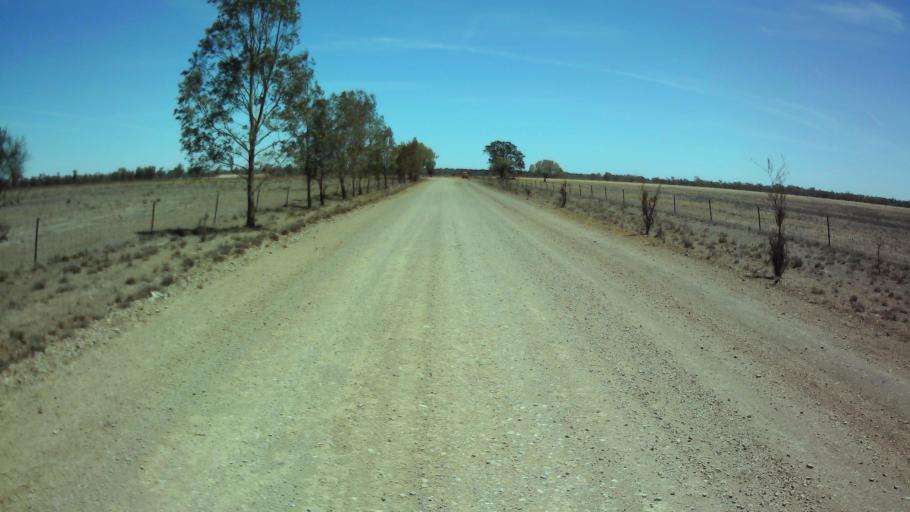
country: AU
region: New South Wales
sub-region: Bland
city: West Wyalong
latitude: -33.8216
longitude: 147.6442
